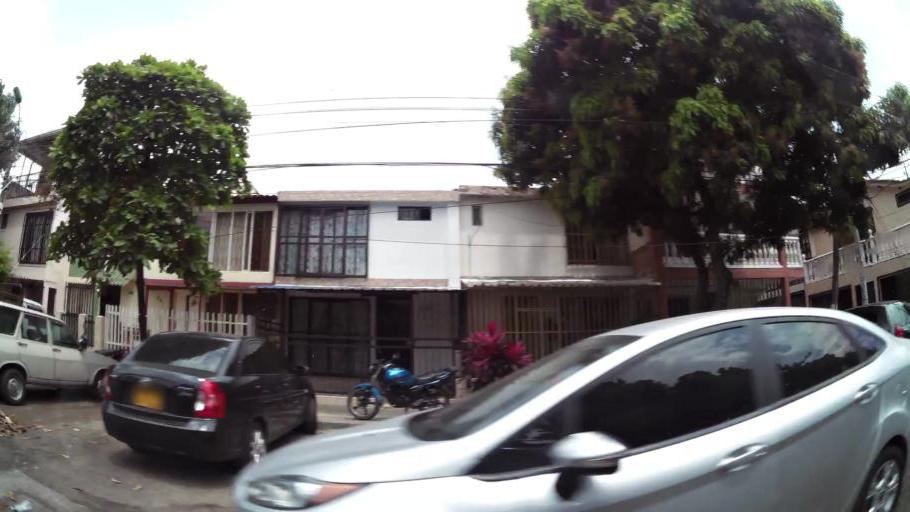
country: CO
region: Valle del Cauca
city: Cali
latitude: 3.4672
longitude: -76.4932
